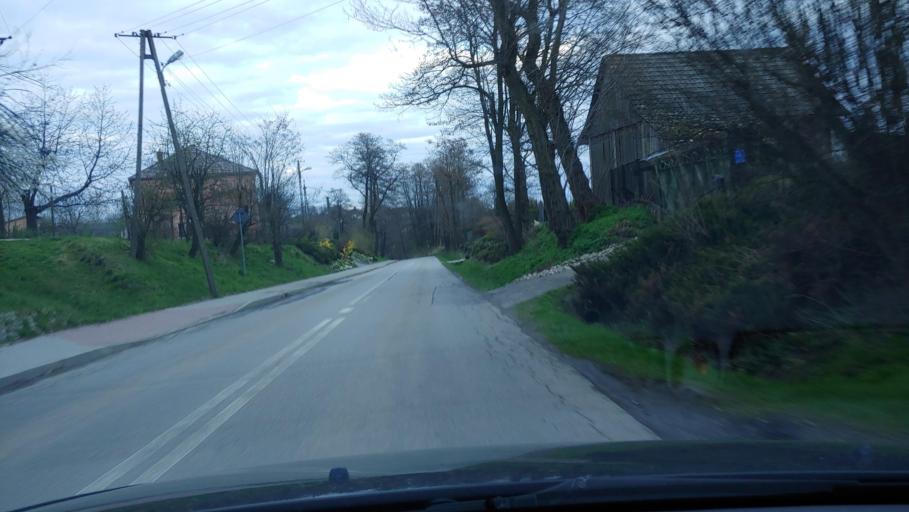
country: PL
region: Lesser Poland Voivodeship
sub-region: Powiat krakowski
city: Rudawa
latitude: 50.1390
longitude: 19.7406
